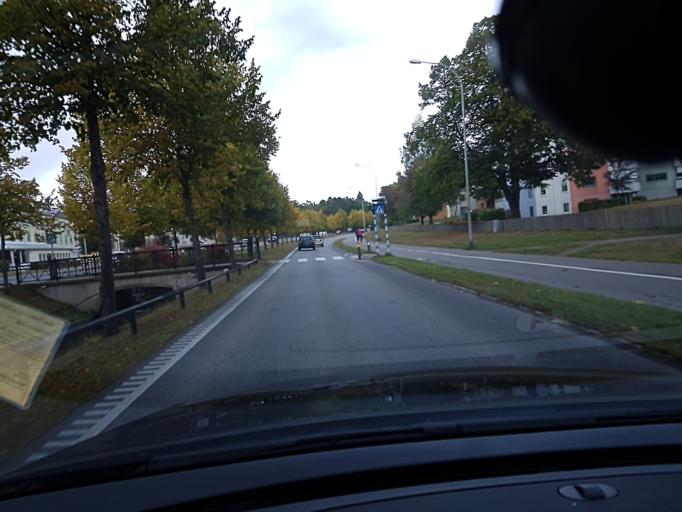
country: SE
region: Kronoberg
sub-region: Vaxjo Kommun
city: Vaexjoe
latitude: 56.8845
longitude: 14.8128
